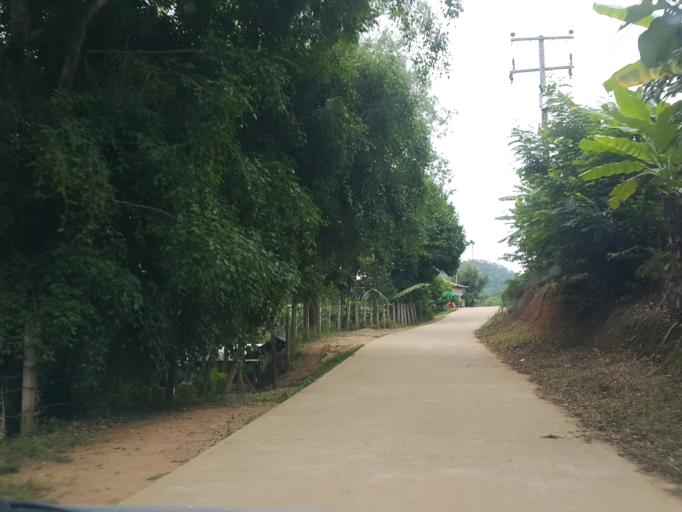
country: TH
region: Chiang Mai
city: Phrao
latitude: 19.3196
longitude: 99.1295
